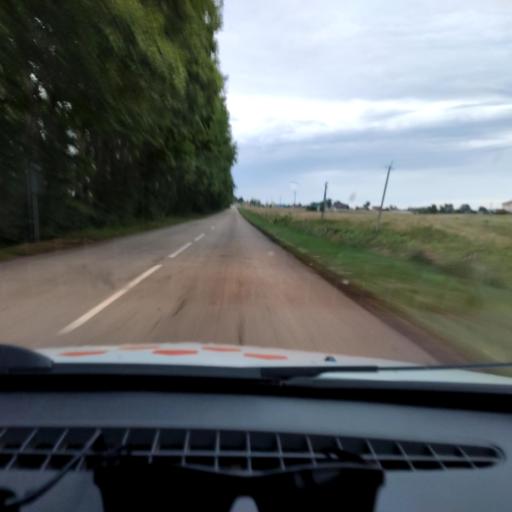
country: RU
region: Bashkortostan
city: Avdon
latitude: 54.4929
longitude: 55.6080
